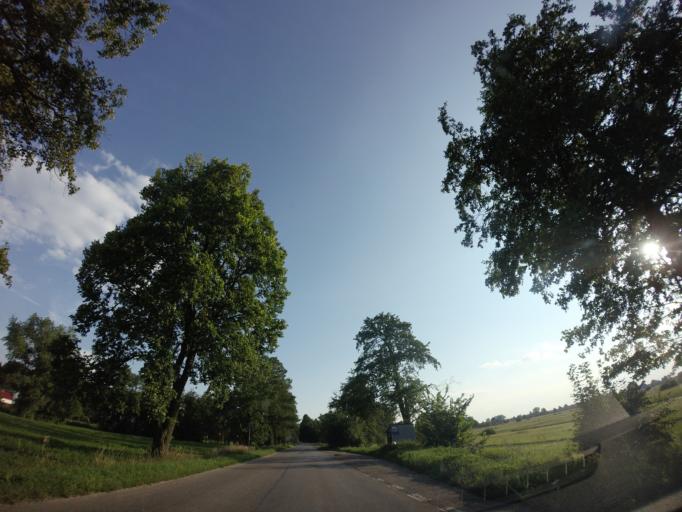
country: PL
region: Lublin Voivodeship
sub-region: Powiat lubartowski
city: Abramow
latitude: 51.4695
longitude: 22.2863
